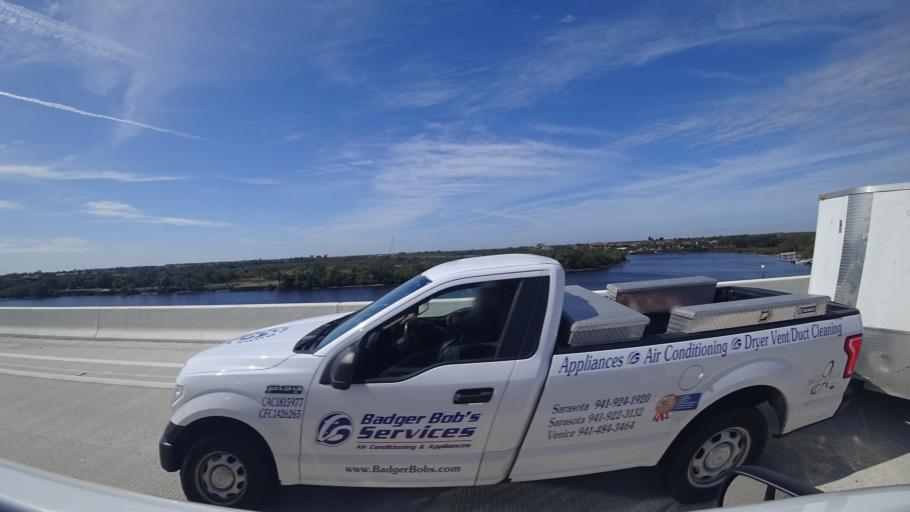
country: US
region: Florida
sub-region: Manatee County
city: Ellenton
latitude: 27.5232
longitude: -82.4284
